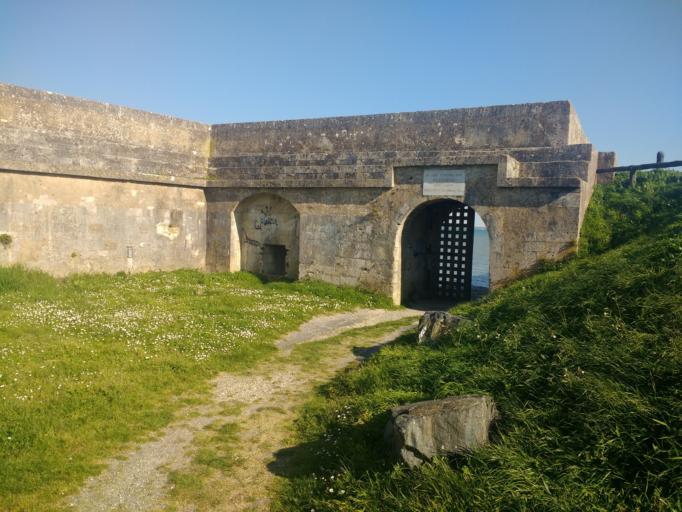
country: FR
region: Poitou-Charentes
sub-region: Departement de la Charente-Maritime
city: Saint-Trojan-les-Bains
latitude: 45.8887
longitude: -1.1914
